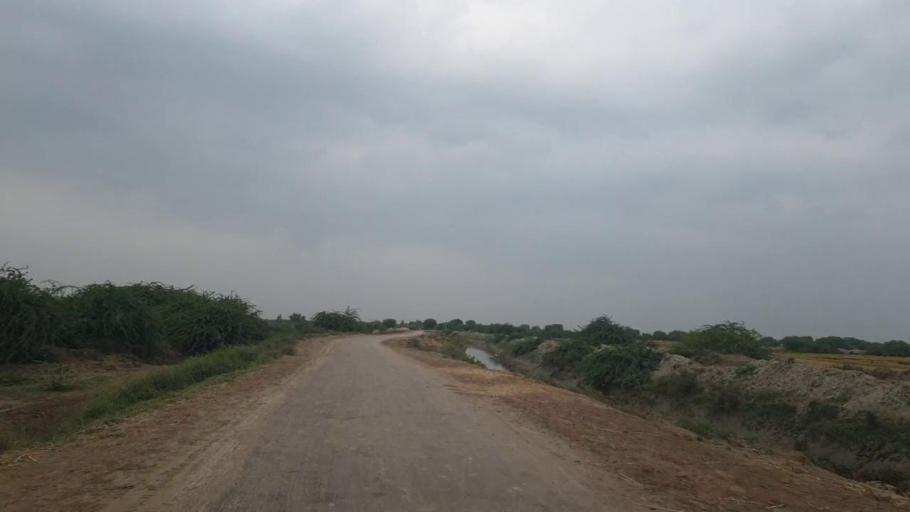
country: PK
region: Sindh
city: Badin
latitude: 24.6271
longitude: 68.6819
